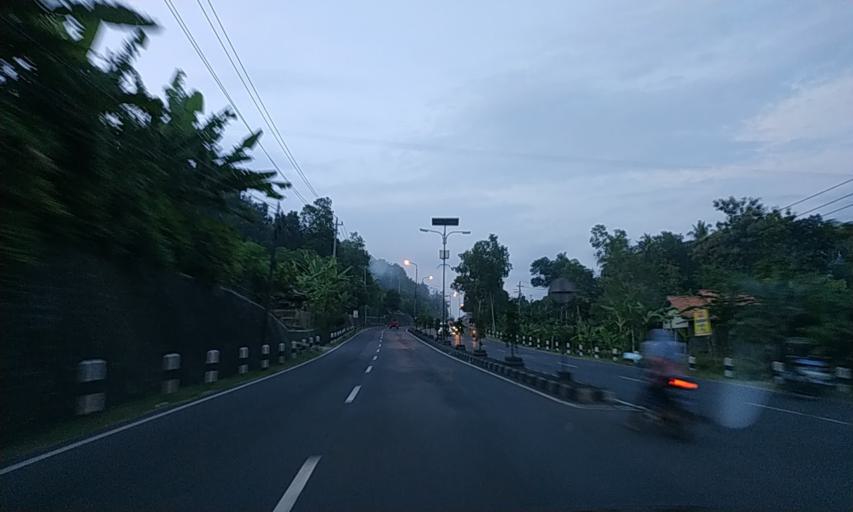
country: ID
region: Daerah Istimewa Yogyakarta
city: Srandakan
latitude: -7.8530
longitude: 110.2161
